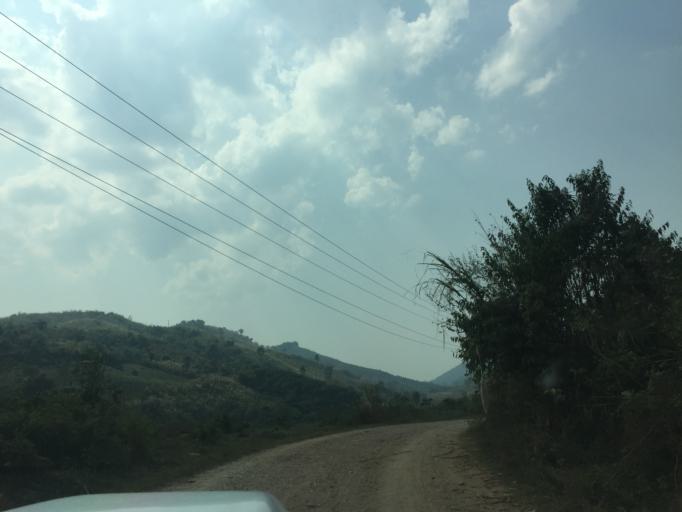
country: TH
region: Nan
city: Song Khwae
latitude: 19.7324
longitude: 100.7291
